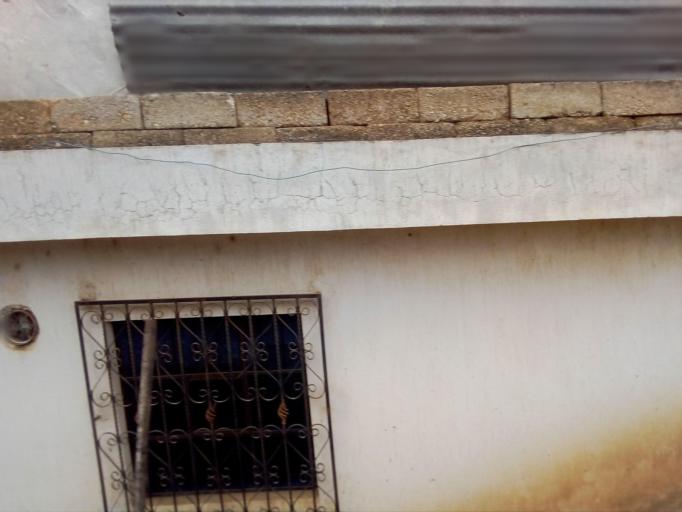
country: GT
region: Quetzaltenango
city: Olintepeque
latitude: 14.8595
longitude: -91.5018
